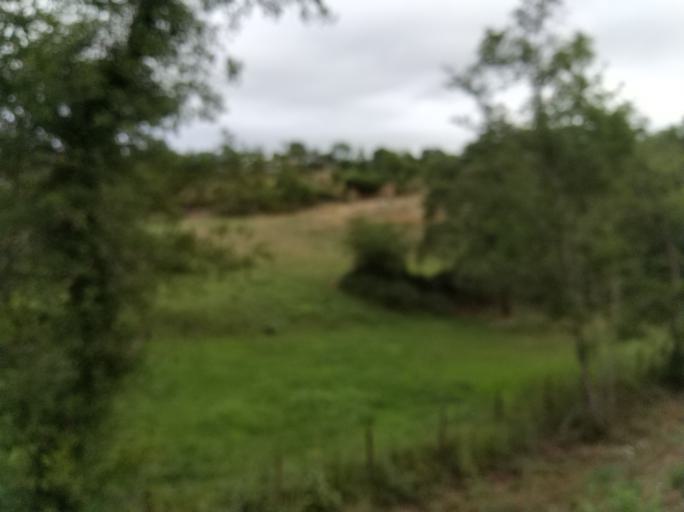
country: FR
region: Rhone-Alpes
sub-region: Departement de l'Ardeche
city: Boulieu-les-Annonay
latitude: 45.2691
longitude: 4.6539
